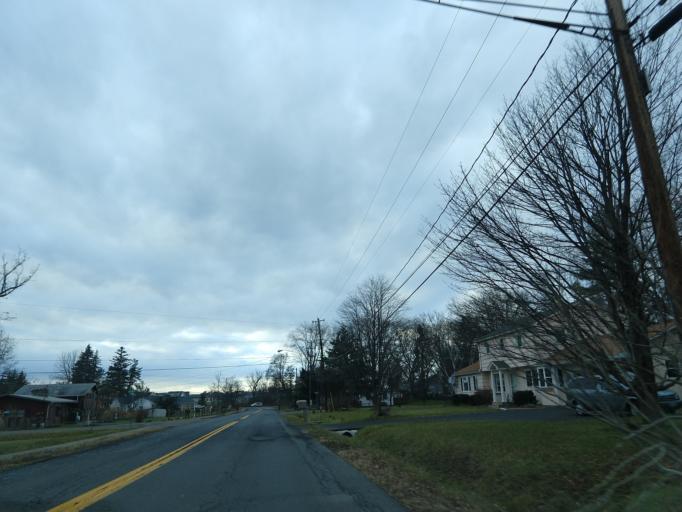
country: US
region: New York
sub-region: Tompkins County
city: Lansing
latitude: 42.4745
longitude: -76.4796
